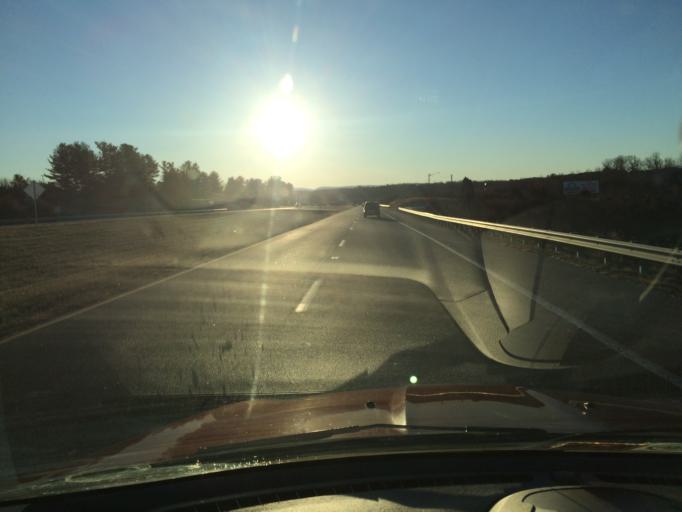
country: US
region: Virginia
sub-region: Augusta County
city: Verona
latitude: 38.1722
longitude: -79.0189
